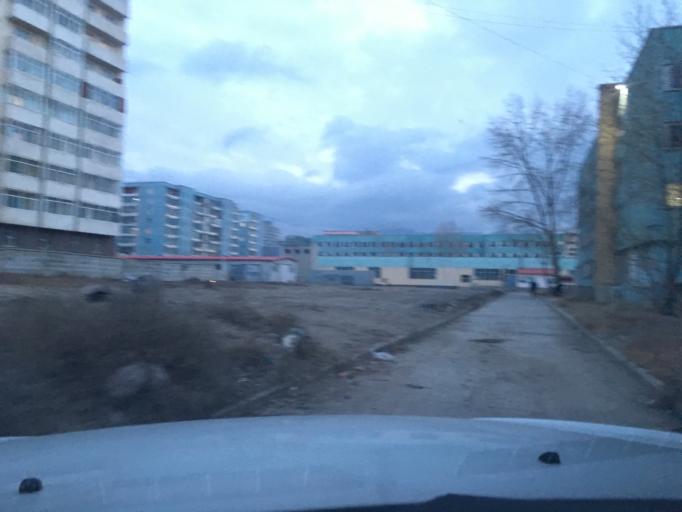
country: MN
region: Ulaanbaatar
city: Ulaanbaatar
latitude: 47.9161
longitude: 106.8610
